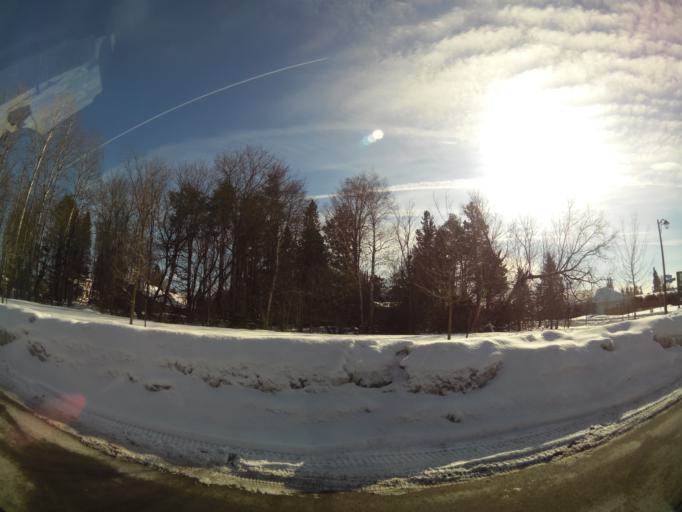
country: CA
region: Ontario
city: Ottawa
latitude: 45.4320
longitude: -75.5141
